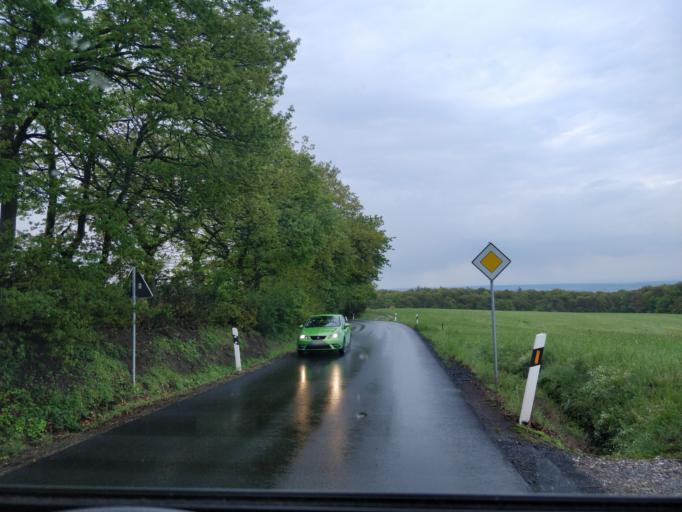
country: DE
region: Rheinland-Pfalz
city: Berg
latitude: 50.5837
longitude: 6.9449
